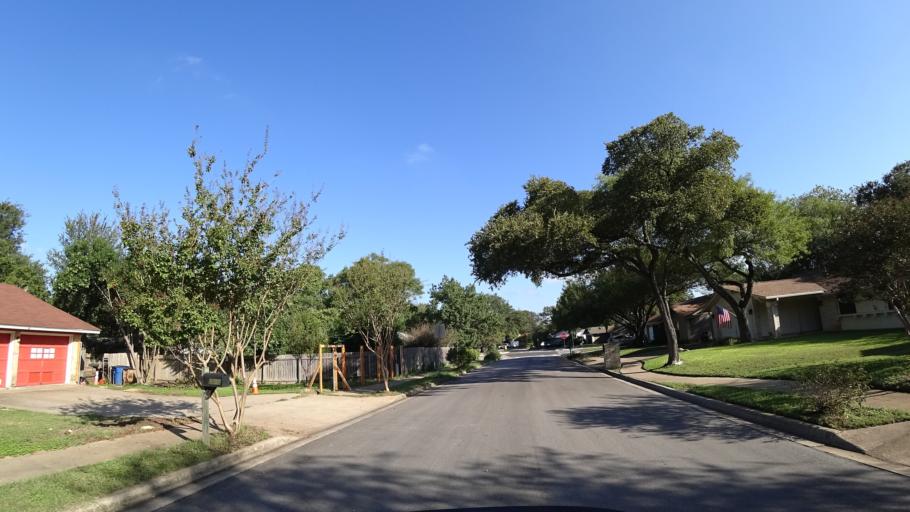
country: US
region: Texas
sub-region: Travis County
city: Rollingwood
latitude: 30.2121
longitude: -97.8089
